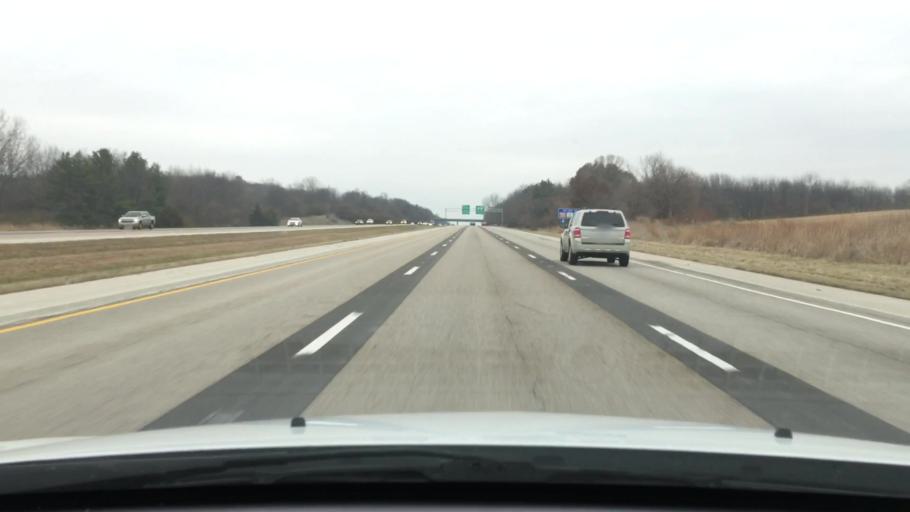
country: US
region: Illinois
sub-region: Logan County
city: Lincoln
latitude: 40.1389
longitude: -89.4170
